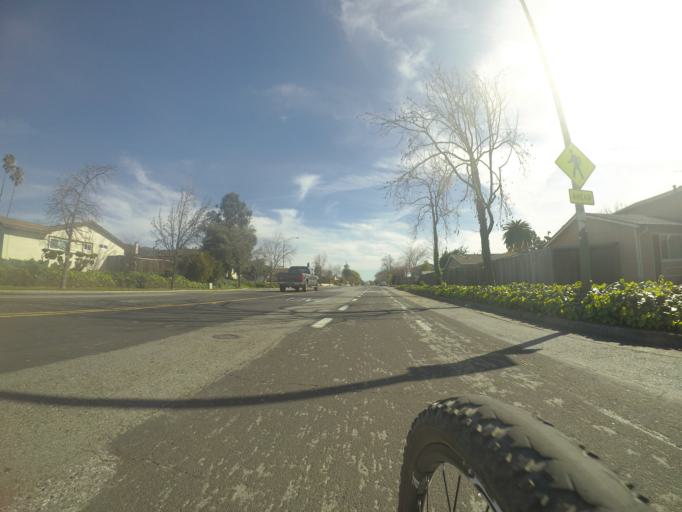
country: US
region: California
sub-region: Santa Clara County
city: Milpitas
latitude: 37.4200
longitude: -121.8596
